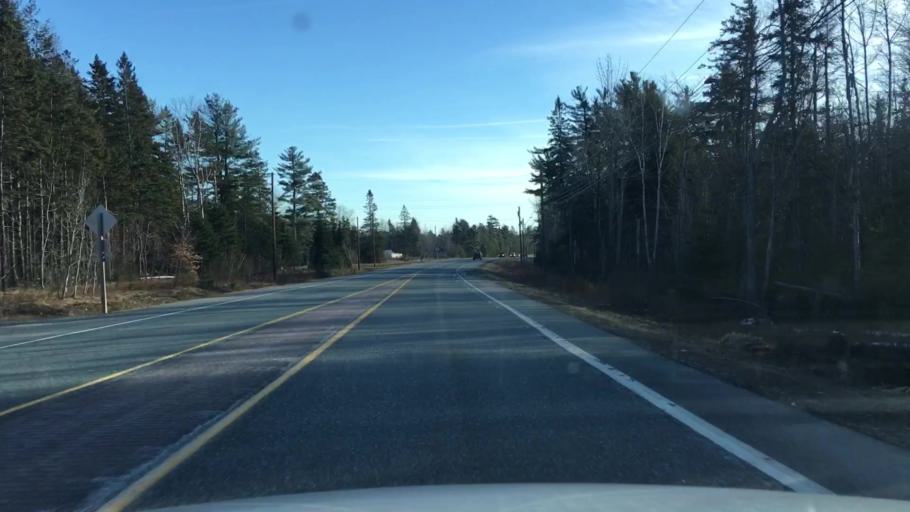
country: US
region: Maine
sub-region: Hancock County
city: Surry
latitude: 44.6137
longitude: -68.5233
